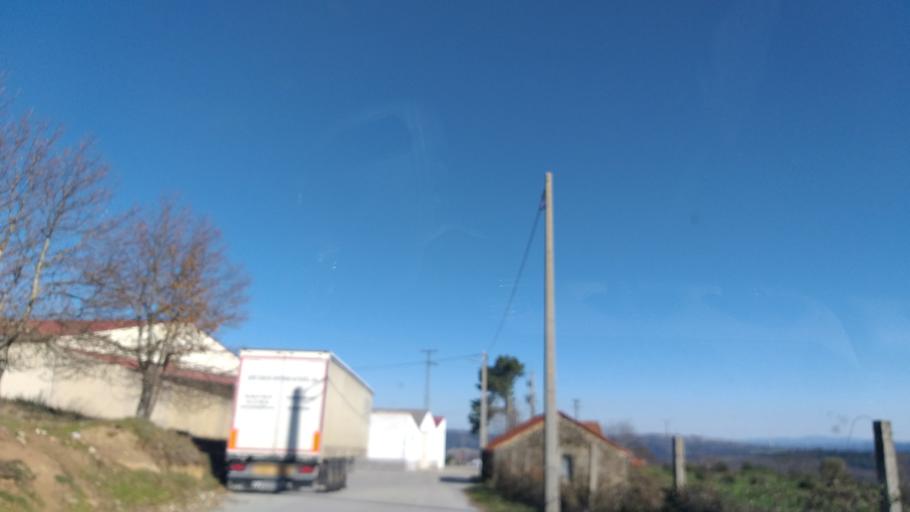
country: PT
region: Guarda
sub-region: Celorico da Beira
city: Celorico da Beira
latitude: 40.5168
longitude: -7.4039
